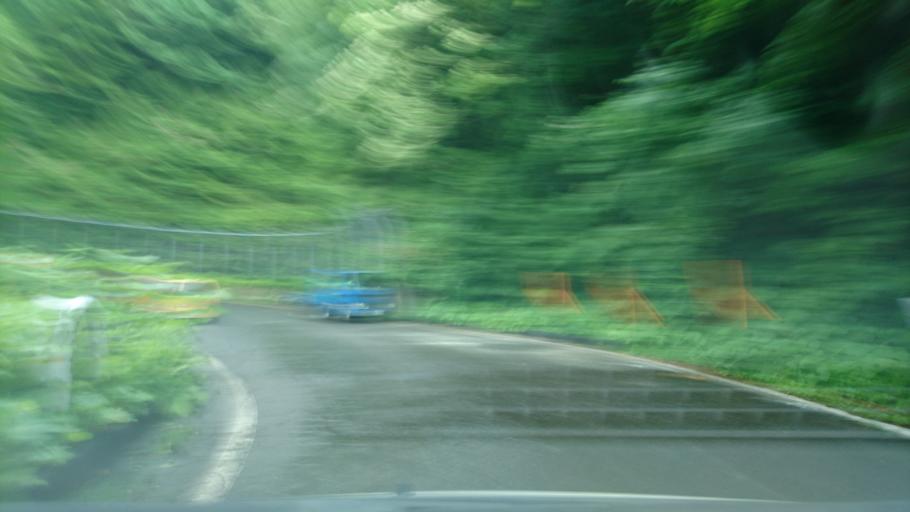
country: JP
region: Iwate
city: Ichinoseki
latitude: 38.9966
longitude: 140.8322
